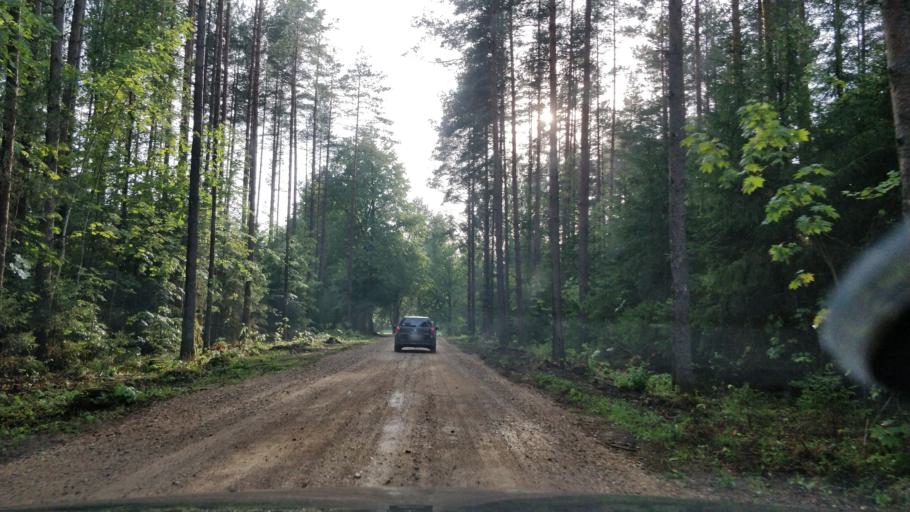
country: LV
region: Sigulda
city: Sigulda
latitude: 57.1000
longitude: 24.8049
